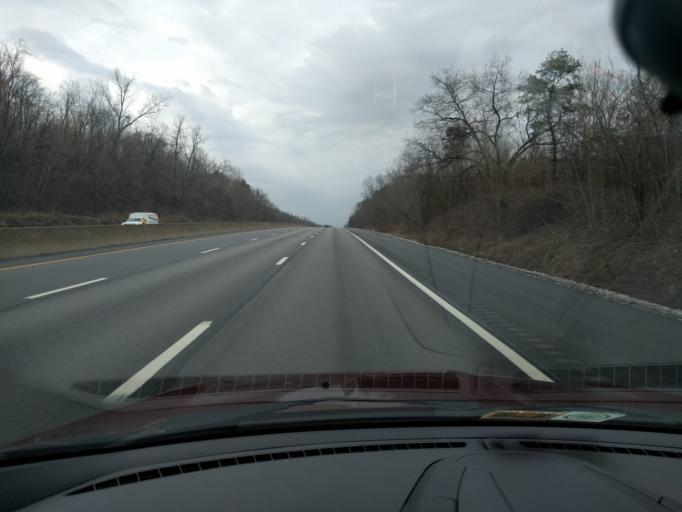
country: US
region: West Virginia
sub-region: Wood County
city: Parkersburg
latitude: 39.2536
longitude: -81.5004
